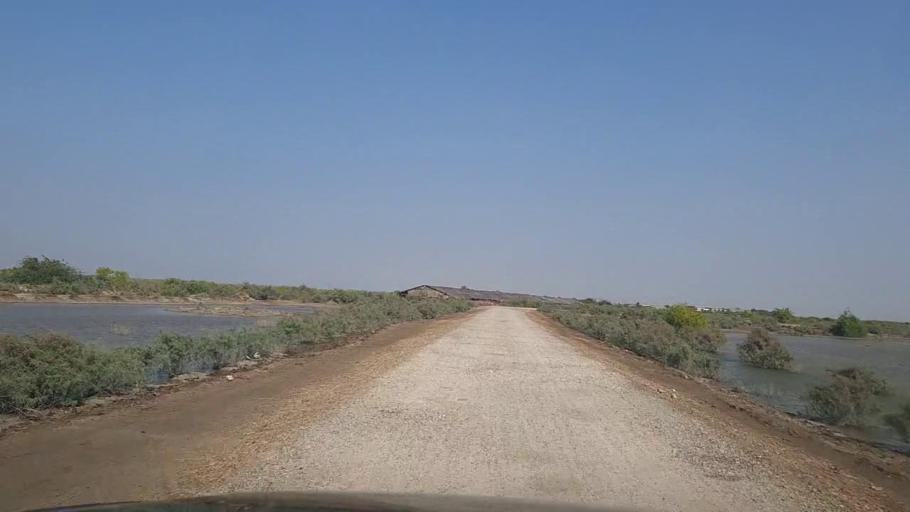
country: PK
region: Sindh
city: Thatta
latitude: 24.6439
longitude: 67.8157
